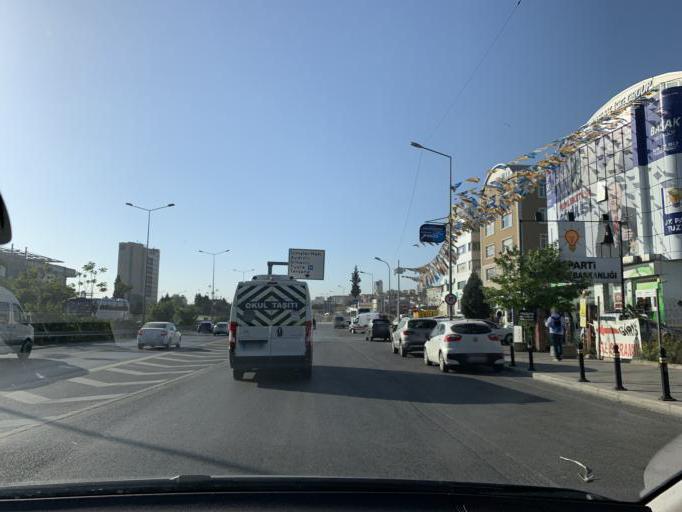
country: TR
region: Istanbul
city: Icmeler
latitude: 40.8474
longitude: 29.3006
